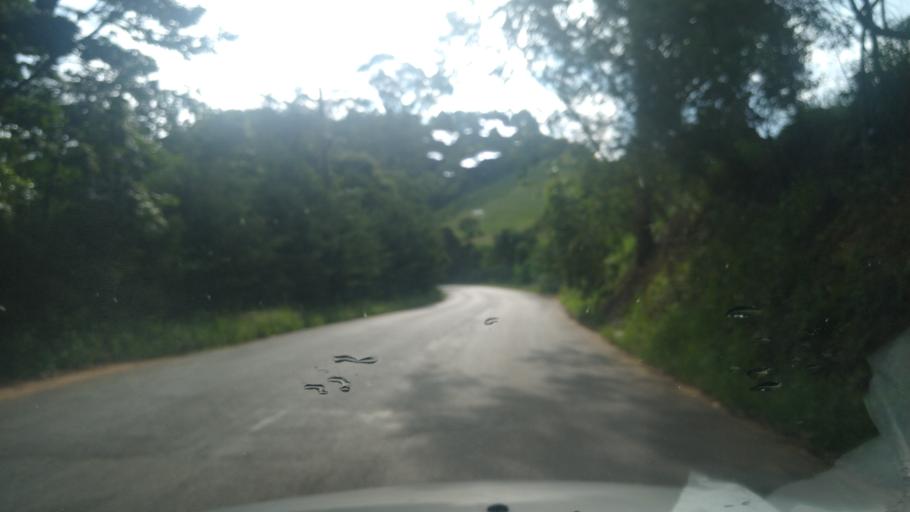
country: BR
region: Minas Gerais
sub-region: Extrema
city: Extrema
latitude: -22.7362
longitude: -46.3682
